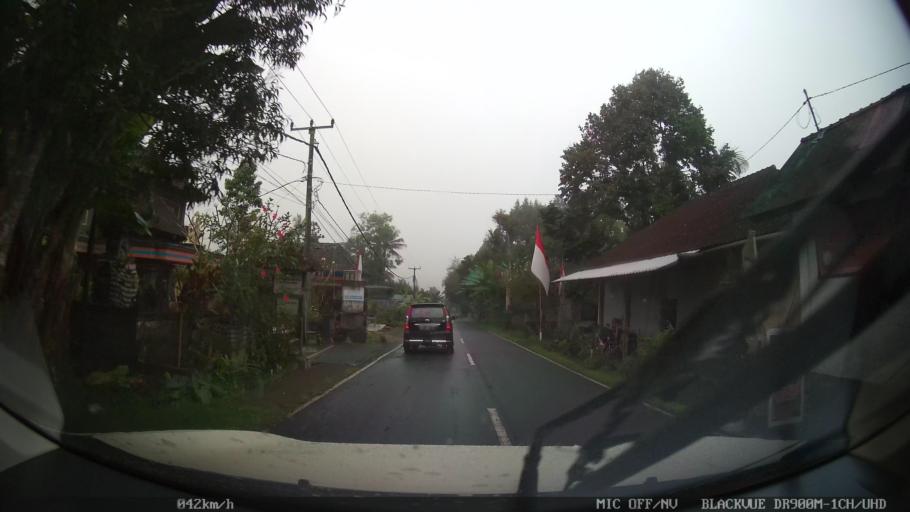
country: ID
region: Bali
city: Banjar Taro Kelod
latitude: -8.3529
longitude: 115.2774
